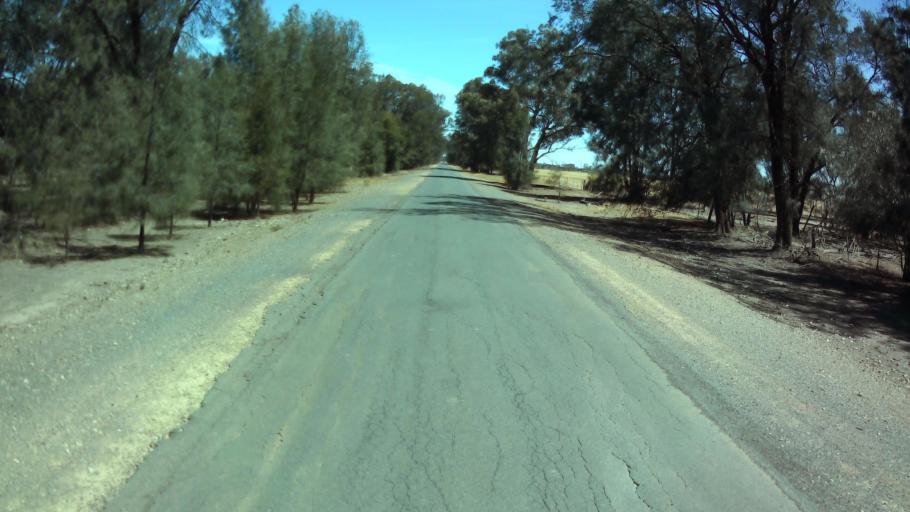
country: AU
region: New South Wales
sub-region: Weddin
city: Grenfell
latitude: -33.8792
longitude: 147.6904
